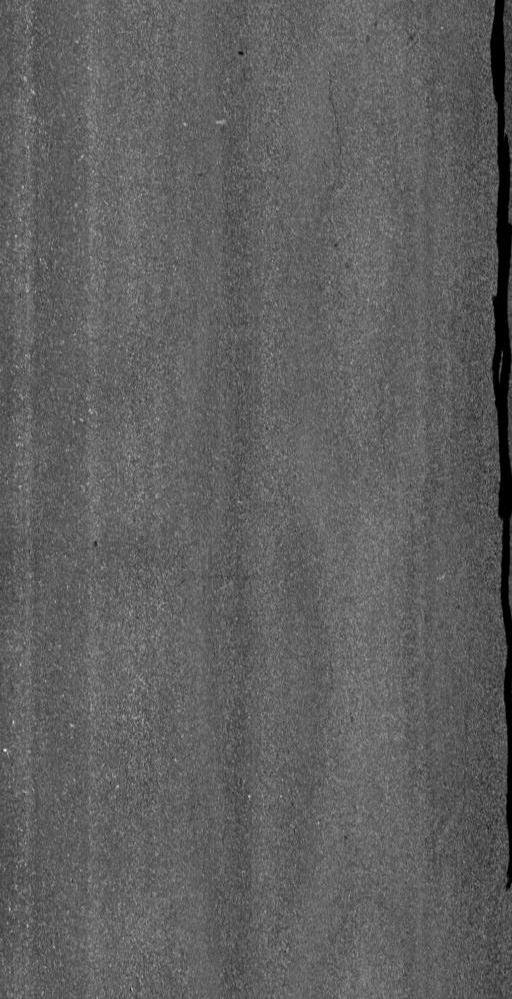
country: US
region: Vermont
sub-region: Chittenden County
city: Burlington
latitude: 44.5230
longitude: -73.2655
